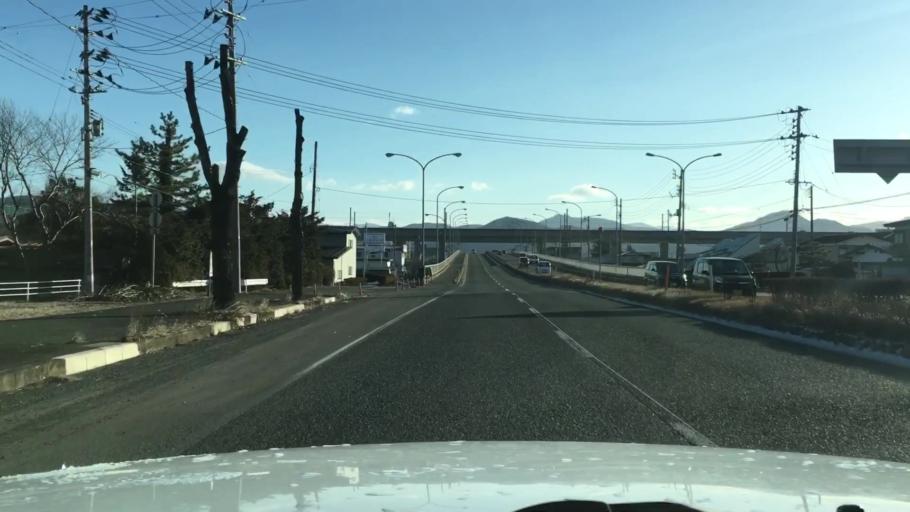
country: JP
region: Iwate
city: Morioka-shi
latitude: 39.6572
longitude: 141.1429
